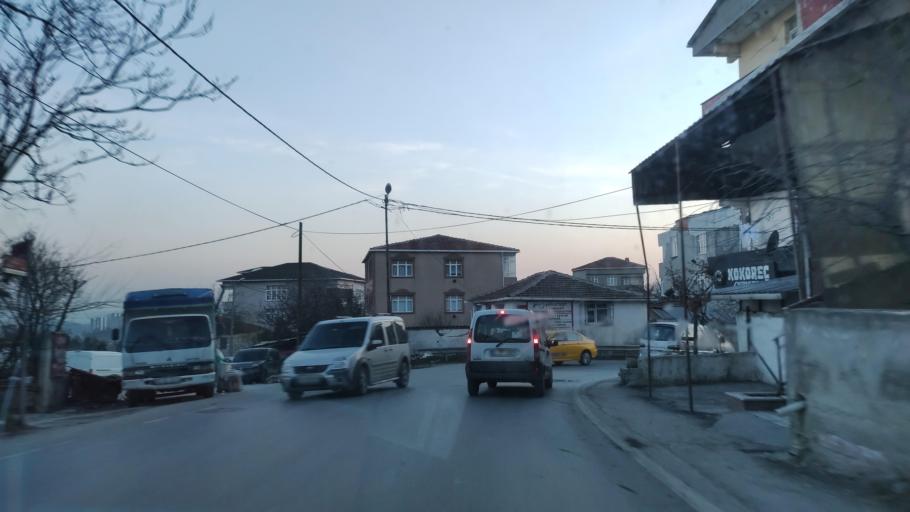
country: TR
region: Istanbul
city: Basaksehir
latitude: 41.1114
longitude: 28.7428
